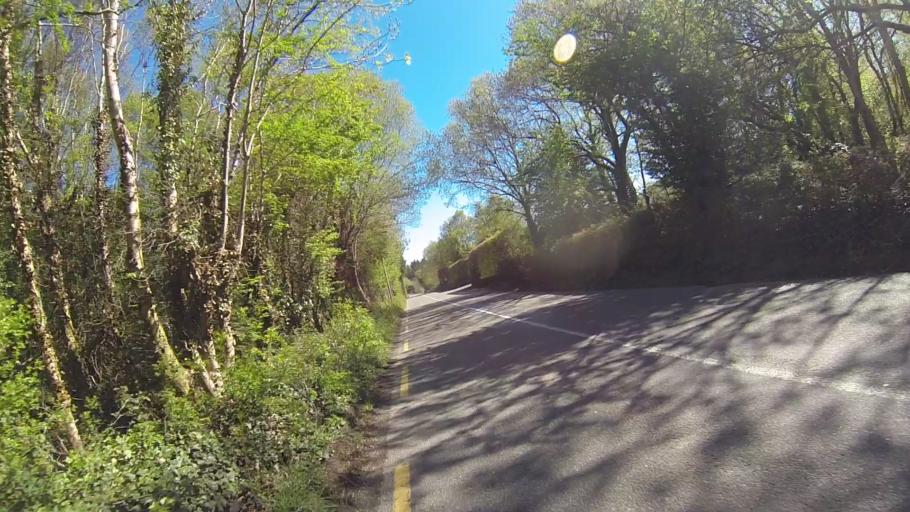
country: IE
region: Munster
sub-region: Ciarrai
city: Kenmare
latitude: 51.8516
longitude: -9.6300
